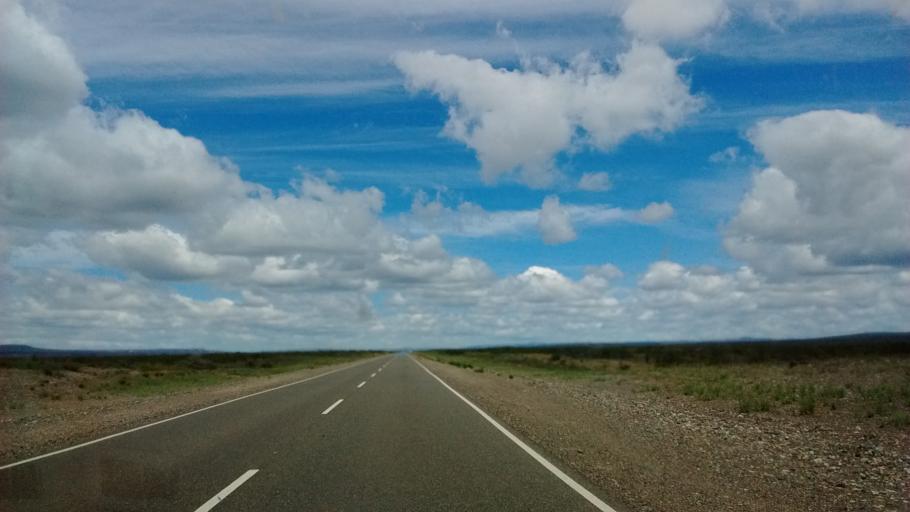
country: AR
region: Neuquen
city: Piedra del Aguila
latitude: -39.8063
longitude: -69.7059
